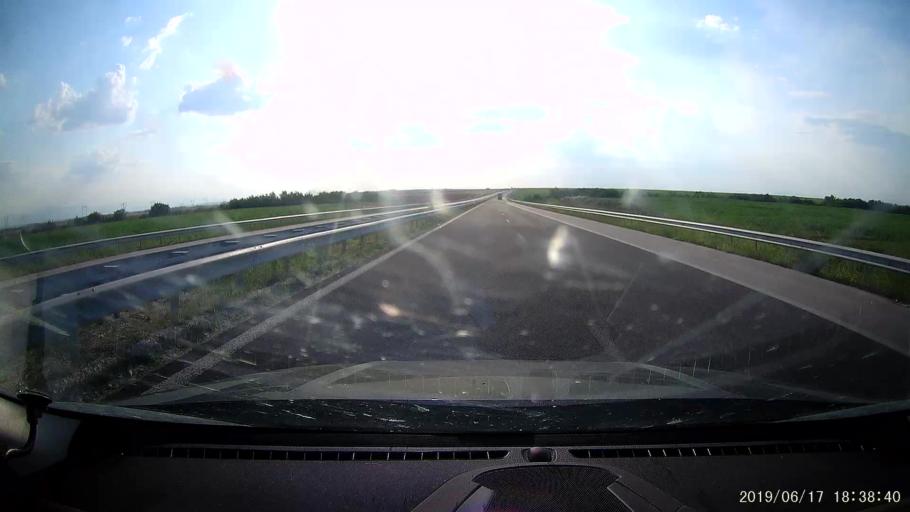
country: BG
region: Stara Zagora
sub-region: Obshtina Chirpan
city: Chirpan
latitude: 42.1384
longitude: 25.3303
